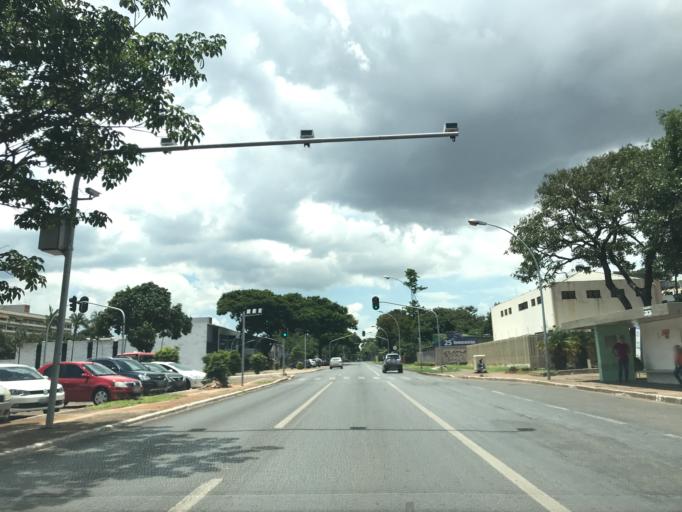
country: BR
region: Federal District
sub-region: Brasilia
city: Brasilia
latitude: -15.8211
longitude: -47.9183
